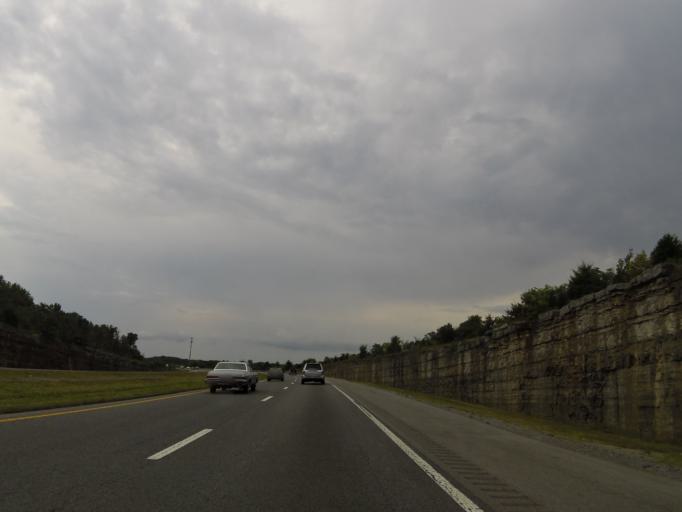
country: US
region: Tennessee
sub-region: Rutherford County
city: Smyrna
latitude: 35.9717
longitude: -86.4480
